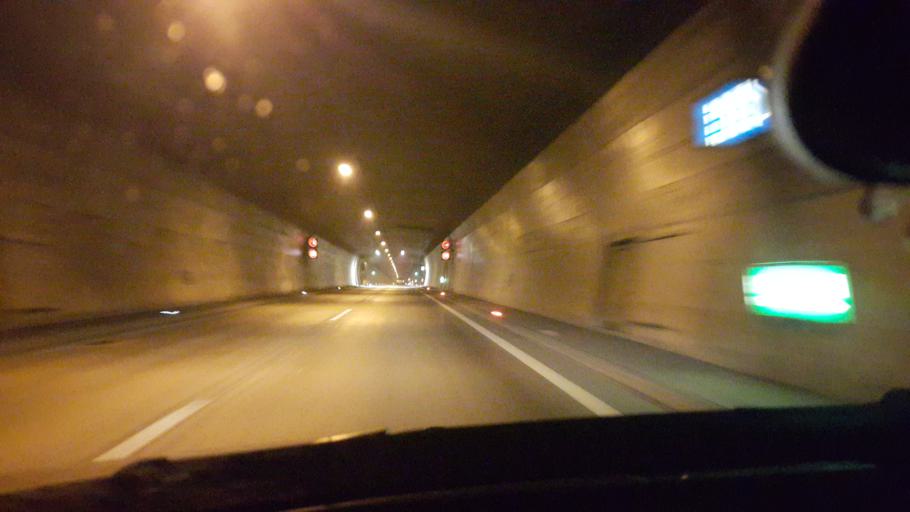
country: AT
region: Styria
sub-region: Graz Stadt
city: Goesting
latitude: 47.0787
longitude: 15.3893
